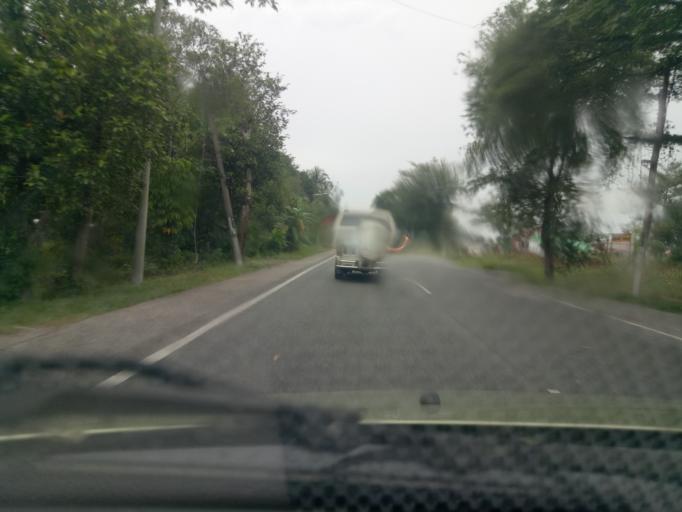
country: MY
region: Kedah
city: Gurun
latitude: 5.9034
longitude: 100.4338
